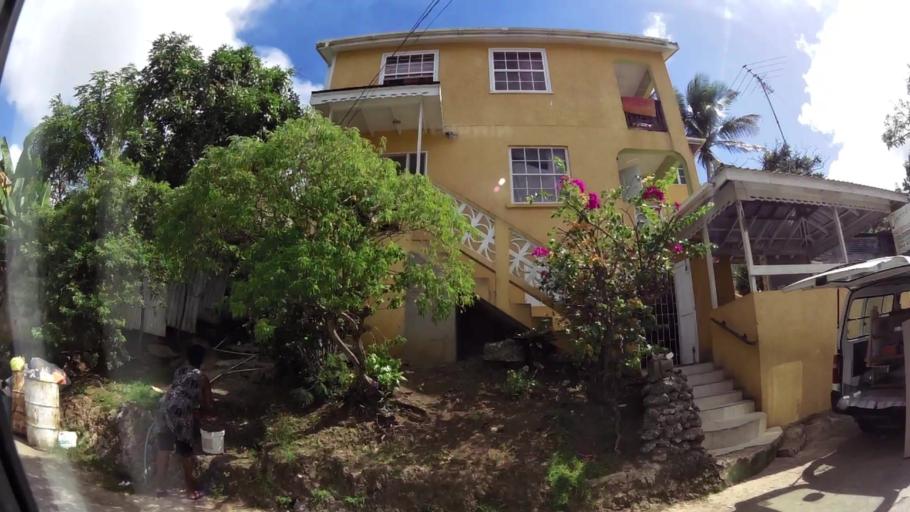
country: BB
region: Saint James
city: Holetown
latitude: 13.2122
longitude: -59.6058
